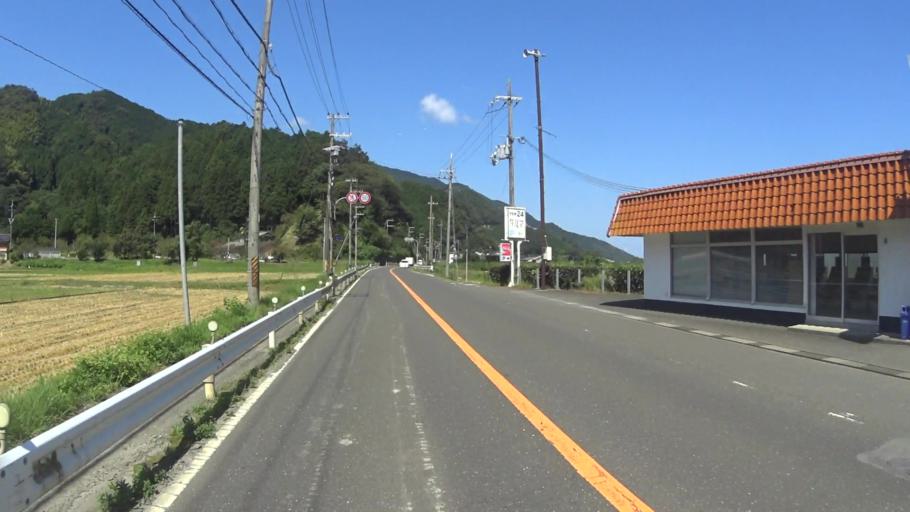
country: JP
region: Kyoto
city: Maizuru
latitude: 35.4707
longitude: 135.2775
